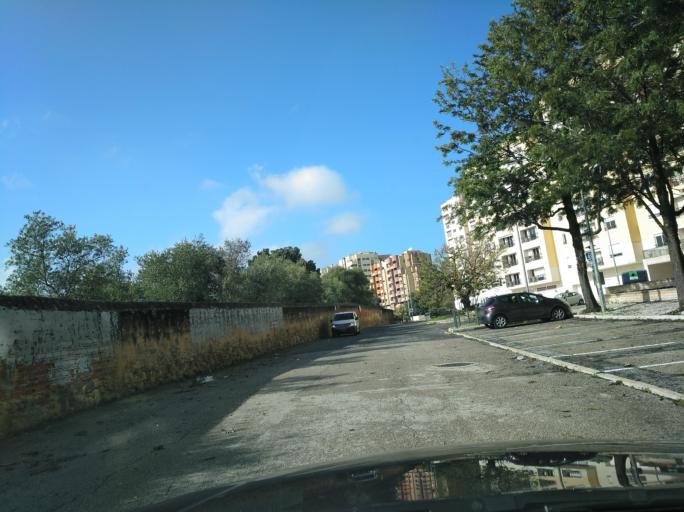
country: PT
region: Lisbon
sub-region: Odivelas
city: Pontinha
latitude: 38.7593
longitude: -9.1764
